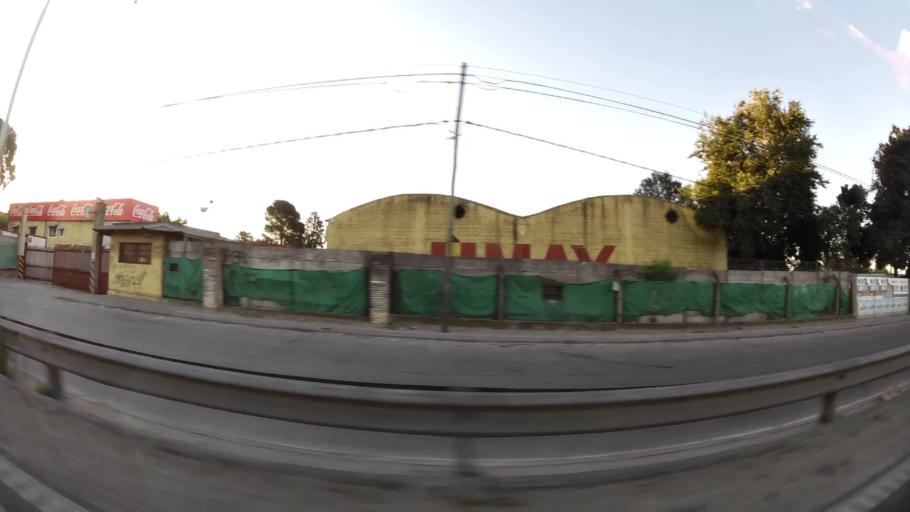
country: AR
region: Buenos Aires
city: Pontevedra
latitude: -34.7890
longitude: -58.6292
